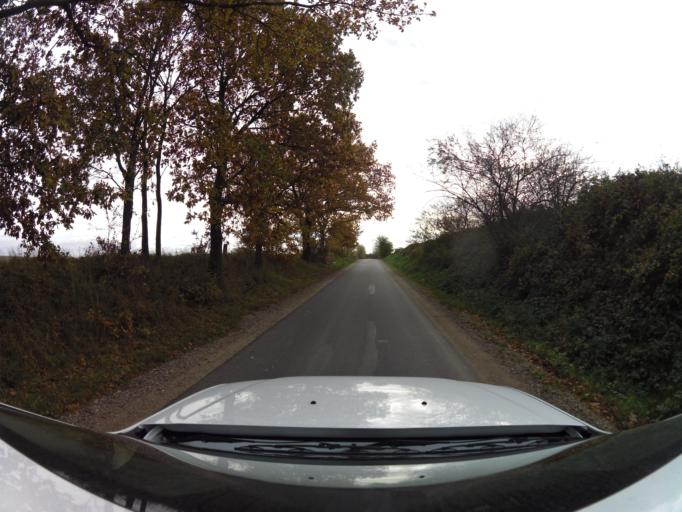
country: PL
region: West Pomeranian Voivodeship
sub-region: Powiat gryficki
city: Cerkwica
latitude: 54.0348
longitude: 15.1532
